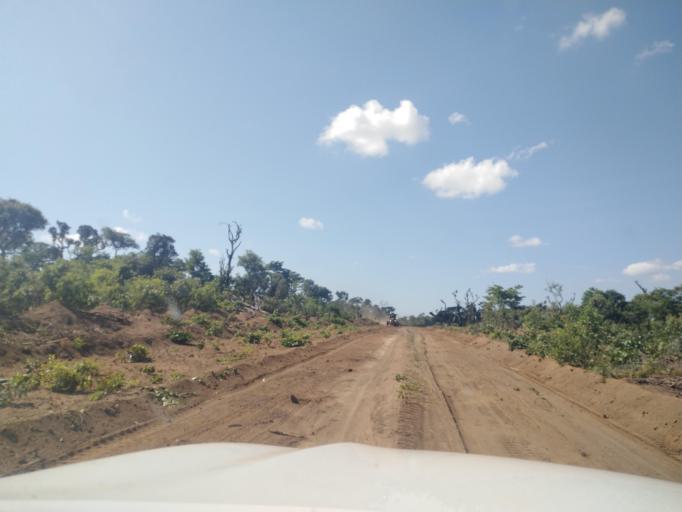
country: ZM
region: Northern
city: Chinsali
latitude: -11.0121
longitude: 31.7735
